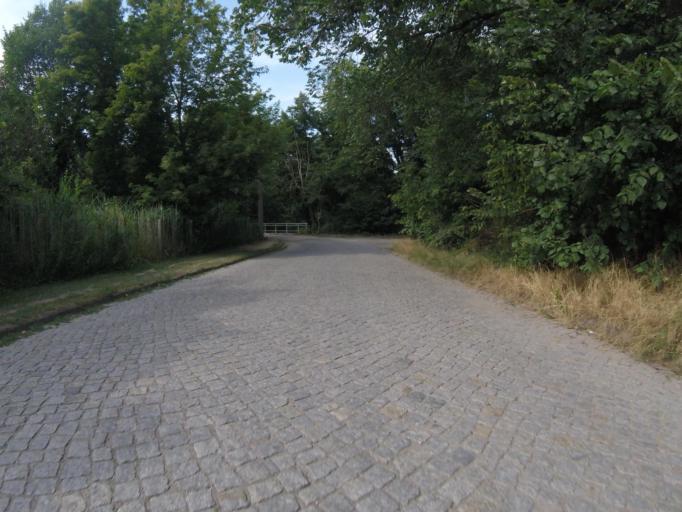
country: DE
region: Brandenburg
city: Wildau
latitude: 52.3193
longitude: 13.7189
